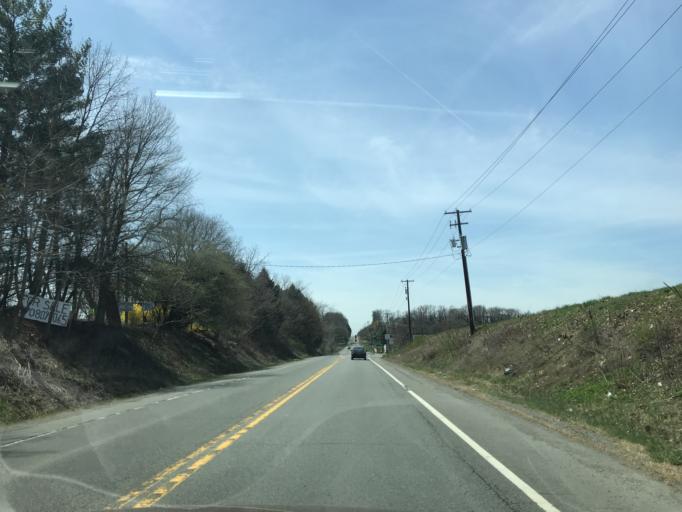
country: US
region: Pennsylvania
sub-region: Snyder County
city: Selinsgrove
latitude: 40.8107
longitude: -76.8622
